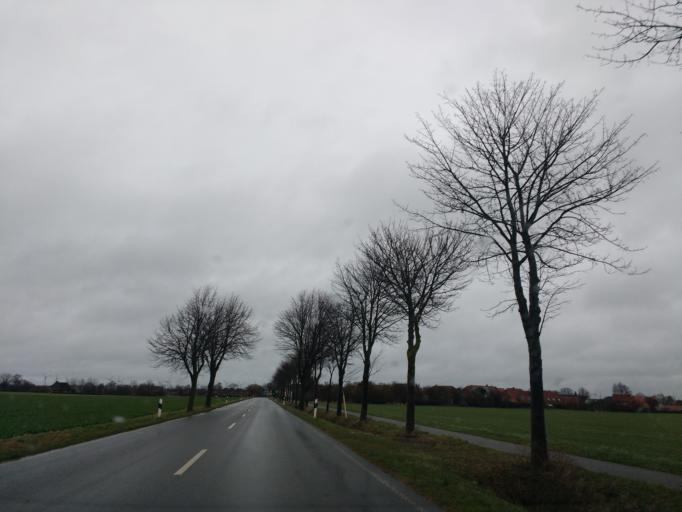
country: DE
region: Schleswig-Holstein
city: Fehmarn
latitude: 54.4529
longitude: 11.2066
